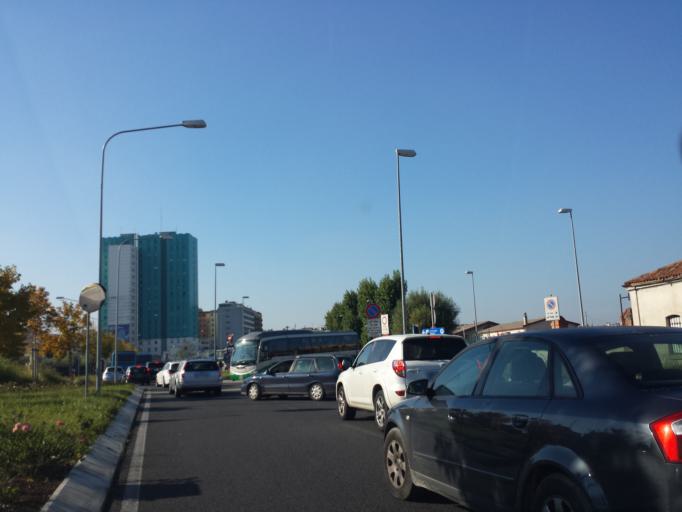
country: IT
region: Veneto
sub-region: Provincia di Padova
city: Padova
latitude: 45.4163
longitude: 11.8854
